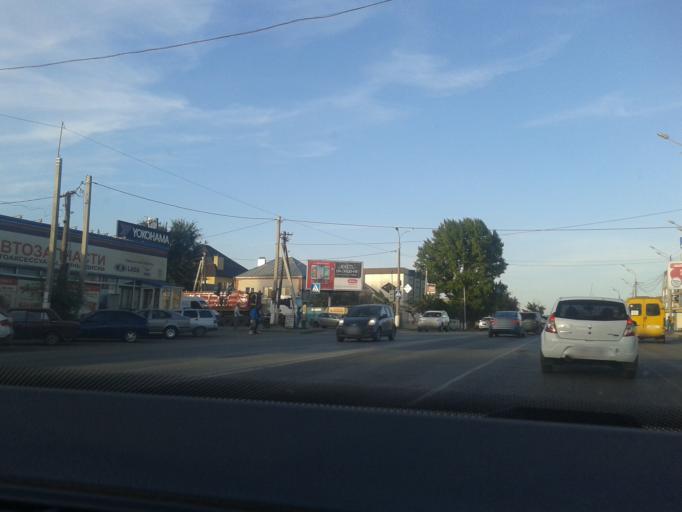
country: RU
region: Volgograd
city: Volgograd
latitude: 48.6959
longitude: 44.4684
